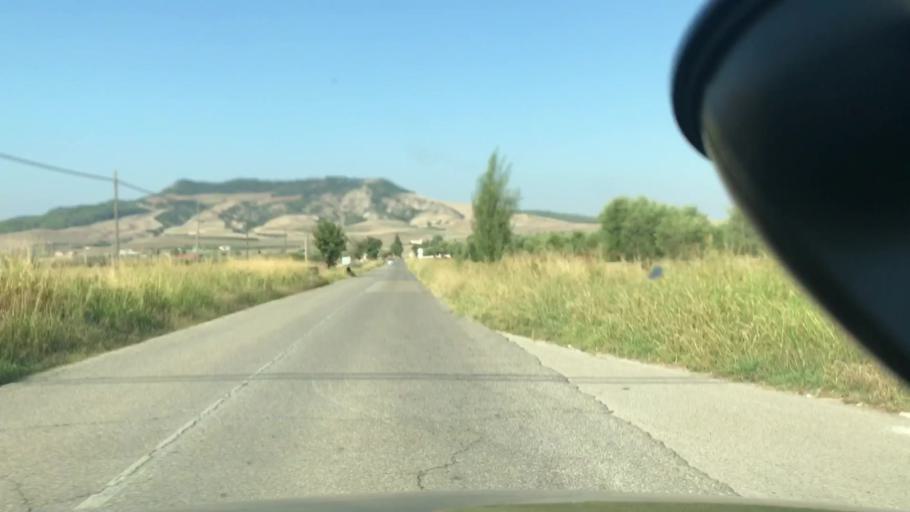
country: IT
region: Basilicate
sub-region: Provincia di Matera
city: La Martella
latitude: 40.6583
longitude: 16.5306
